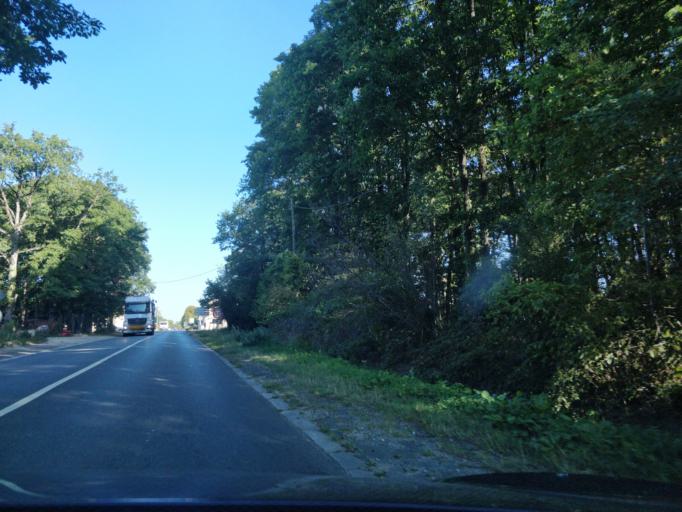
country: FR
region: Ile-de-France
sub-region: Departement de l'Essonne
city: Orsay
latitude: 48.6668
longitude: 2.1972
